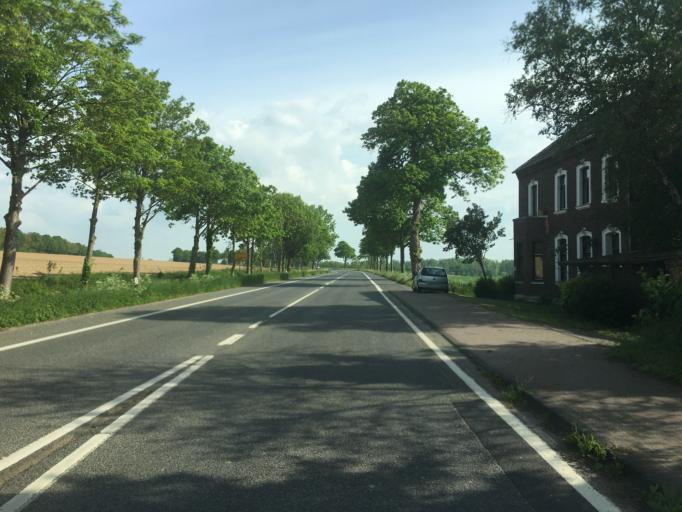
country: DE
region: North Rhine-Westphalia
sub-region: Regierungsbezirk Koln
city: Linnich
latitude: 50.9624
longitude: 6.3213
